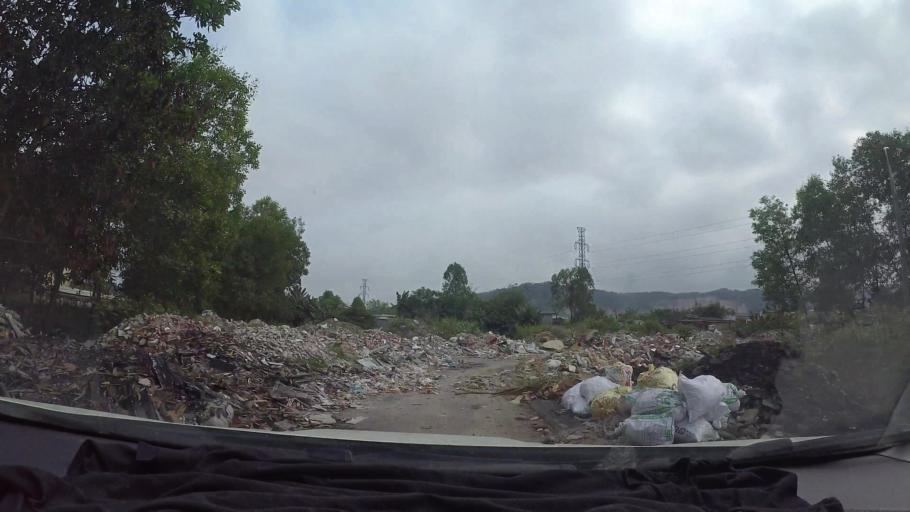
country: VN
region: Da Nang
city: Lien Chieu
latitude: 16.0559
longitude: 108.1612
